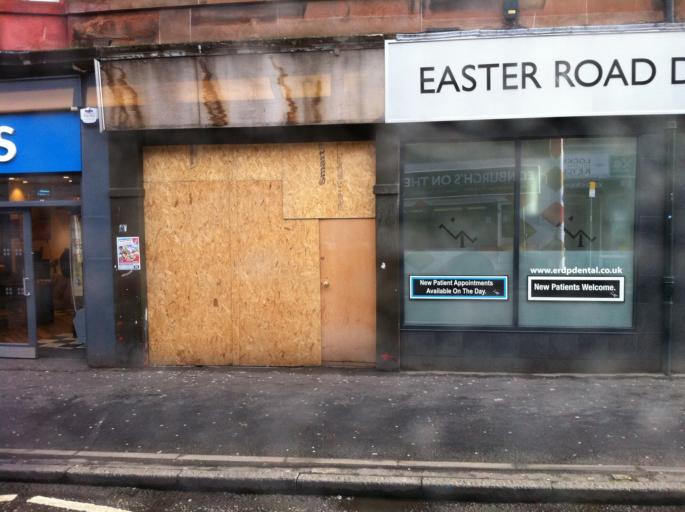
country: GB
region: Scotland
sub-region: West Lothian
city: Seafield
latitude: 55.9589
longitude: -3.1715
